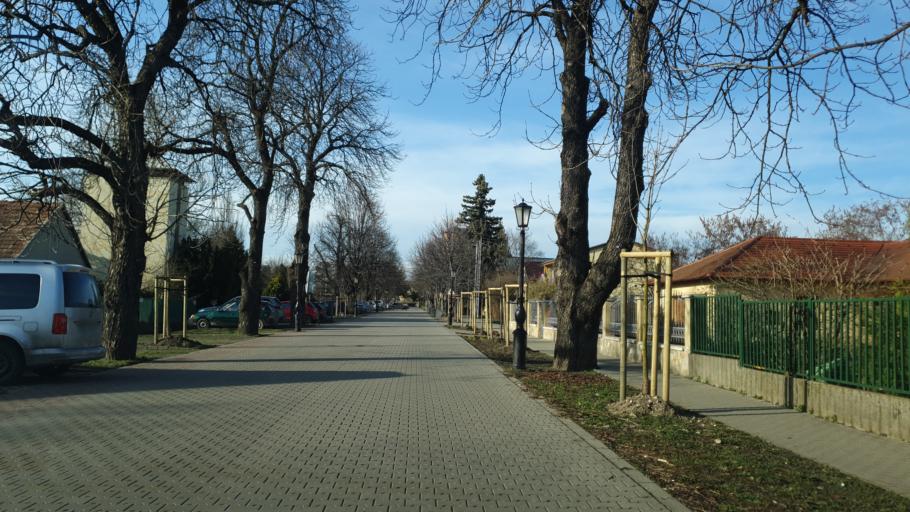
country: HU
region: Fejer
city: Etyek
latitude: 47.5007
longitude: 18.7524
